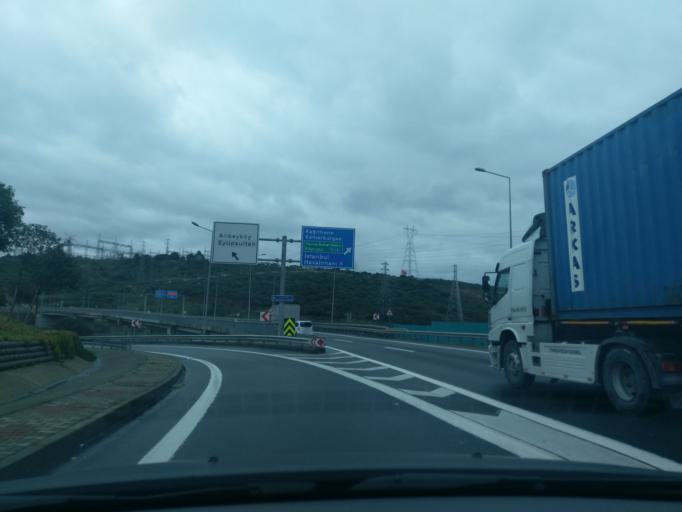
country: TR
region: Istanbul
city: Sisli
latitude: 41.0933
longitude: 28.9513
